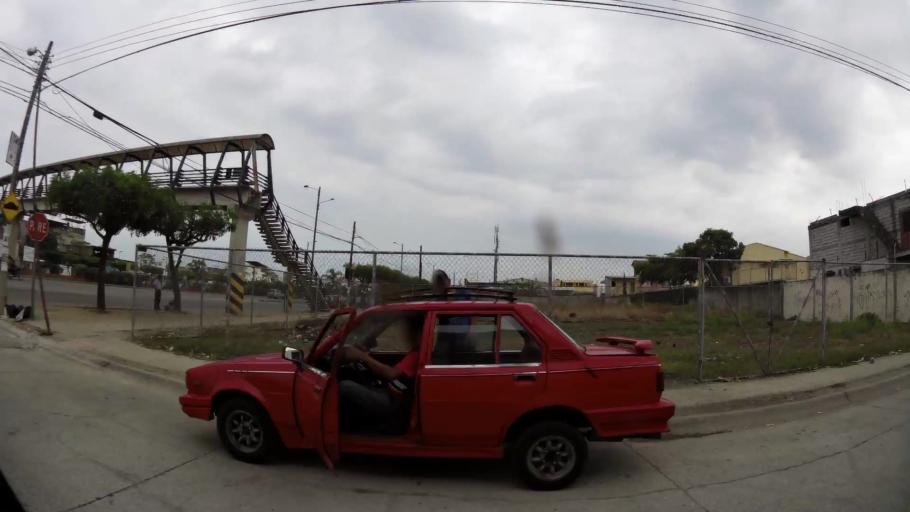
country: EC
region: Guayas
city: Eloy Alfaro
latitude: -2.1318
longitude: -79.8826
